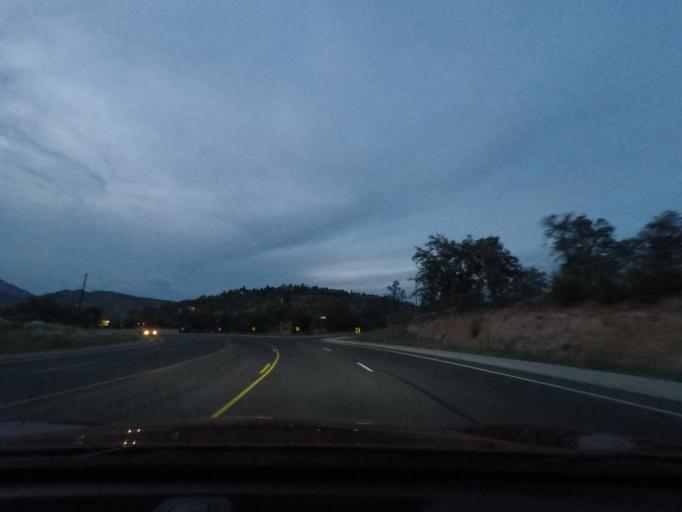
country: US
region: Arizona
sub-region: Yavapai County
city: Prescott
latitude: 34.5775
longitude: -112.4982
